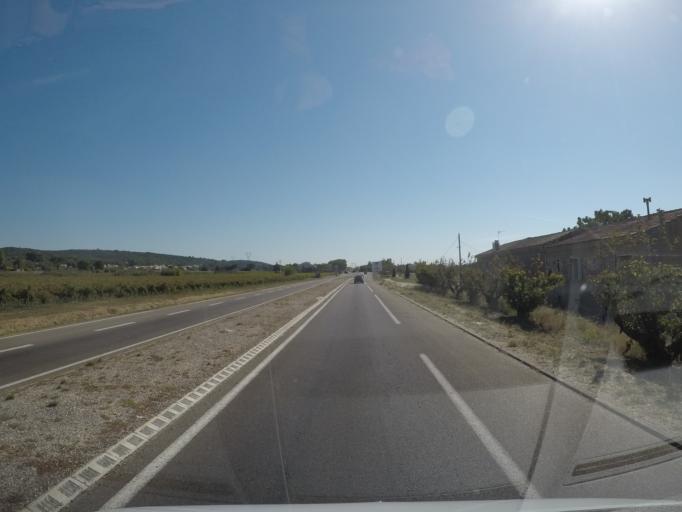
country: FR
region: Languedoc-Roussillon
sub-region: Departement du Gard
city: Uzes
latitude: 43.9879
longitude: 4.4461
